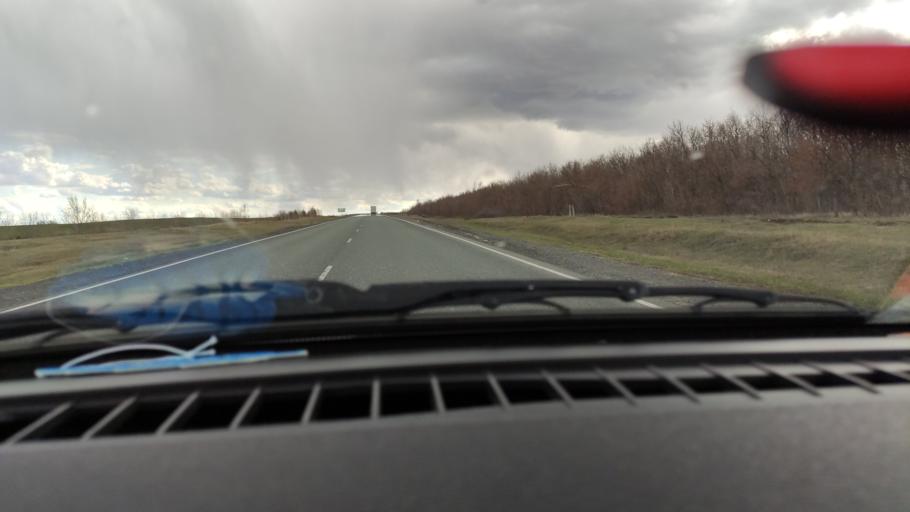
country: RU
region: Saratov
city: Balakovo
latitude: 52.1808
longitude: 47.8417
